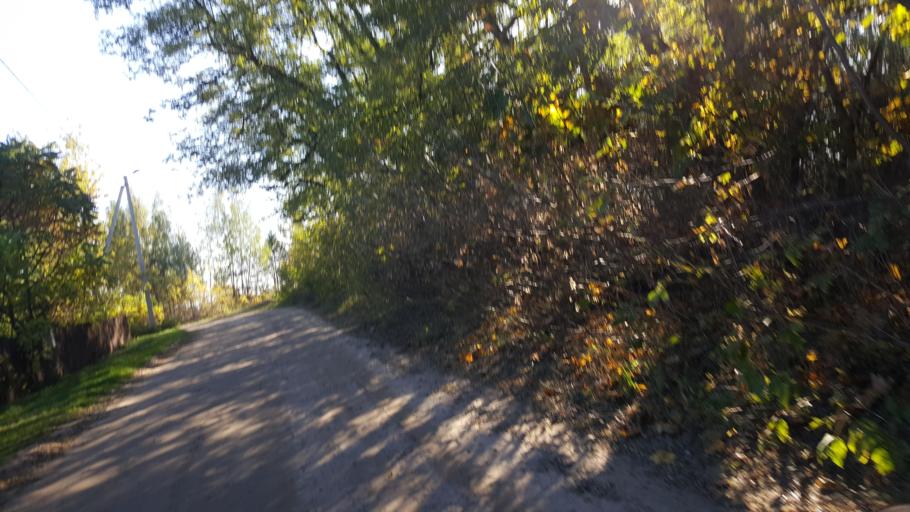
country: BY
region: Brest
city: Kamyanyets
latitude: 52.3900
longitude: 23.8841
